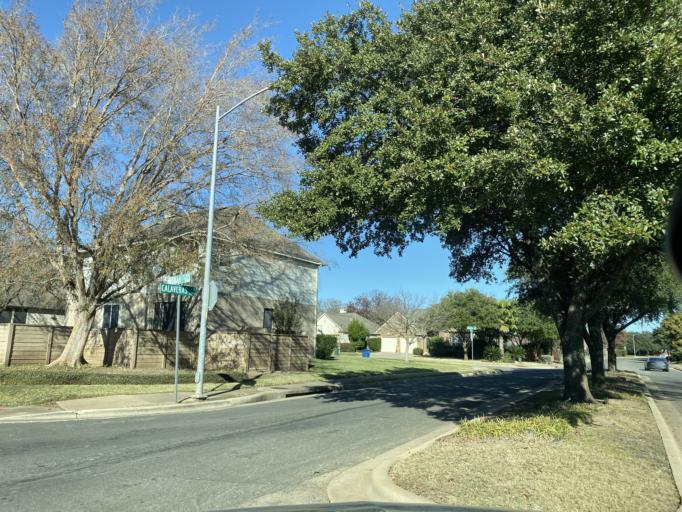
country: US
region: Texas
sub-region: Williamson County
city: Brushy Creek
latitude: 30.4885
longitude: -97.7695
